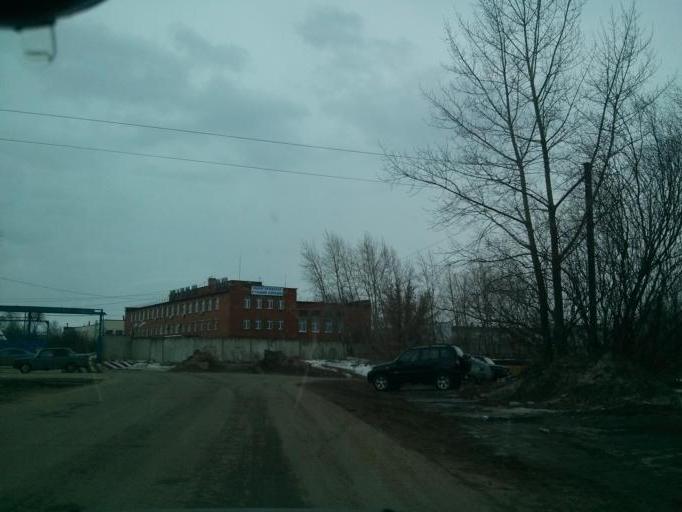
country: RU
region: Nizjnij Novgorod
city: Afonino
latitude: 56.2853
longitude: 44.1194
